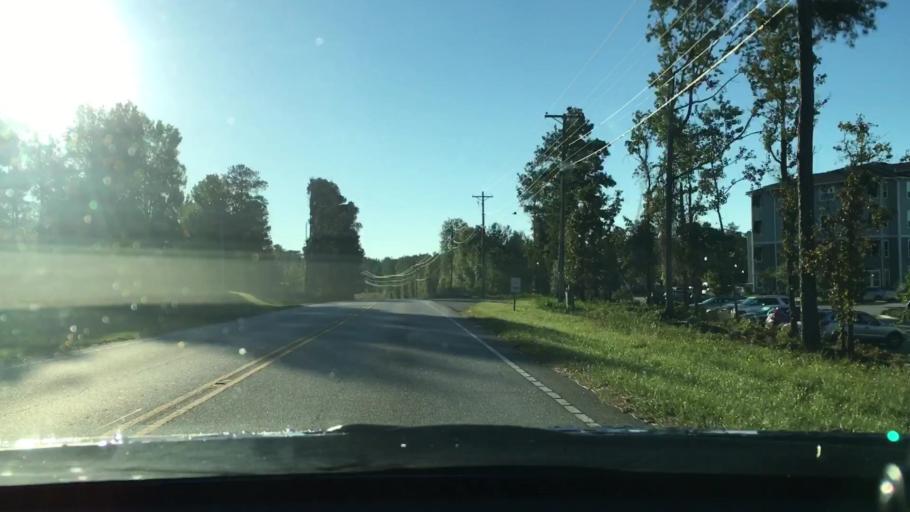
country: US
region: South Carolina
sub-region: Lexington County
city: Irmo
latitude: 34.0912
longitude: -81.1522
